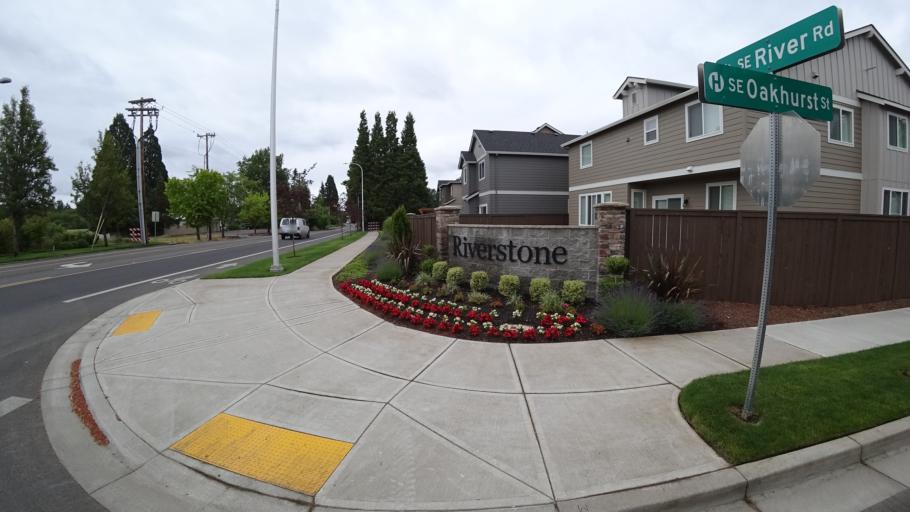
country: US
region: Oregon
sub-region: Washington County
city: Hillsboro
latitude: 45.4913
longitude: -122.9399
